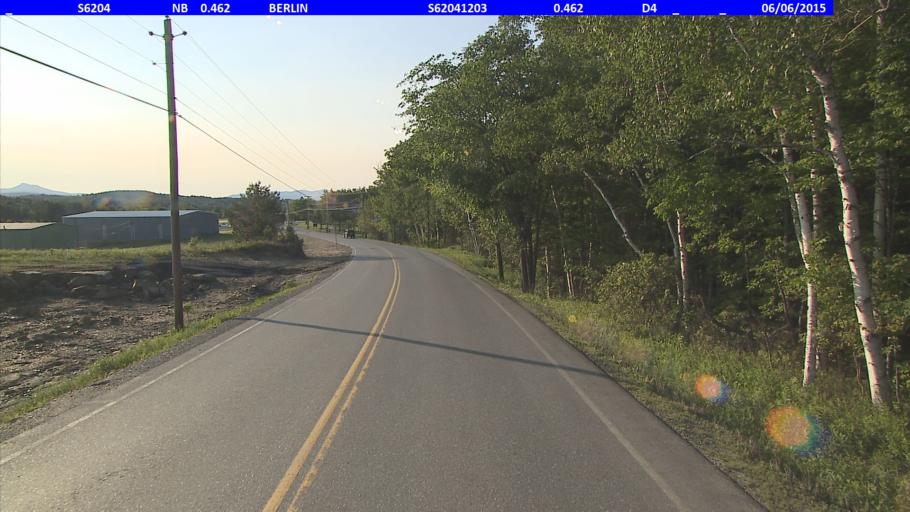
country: US
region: Vermont
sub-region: Washington County
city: Barre
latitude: 44.1988
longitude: -72.5589
